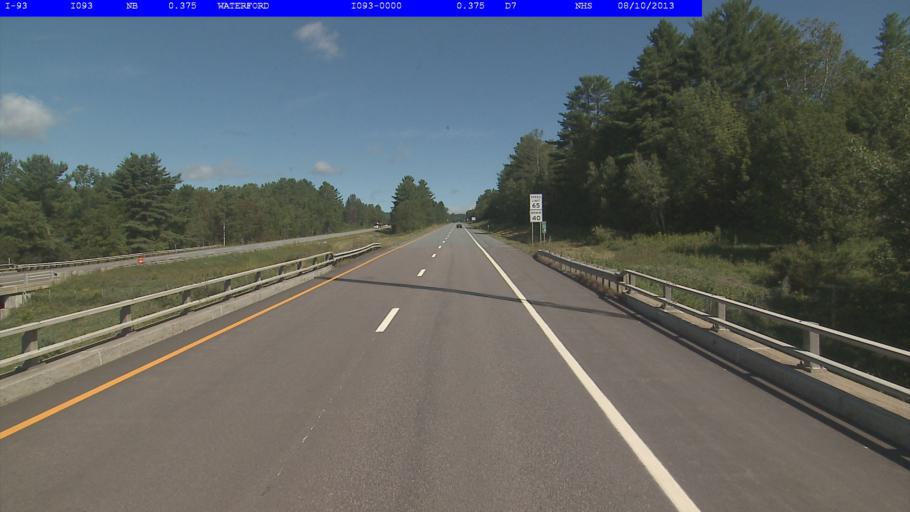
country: US
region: New Hampshire
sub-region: Grafton County
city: Littleton
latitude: 44.3484
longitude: -71.8929
